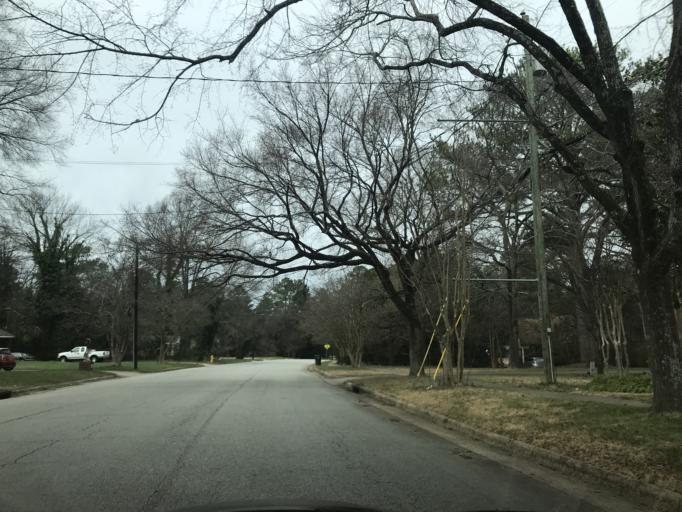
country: US
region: North Carolina
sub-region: Wake County
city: Raleigh
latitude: 35.7813
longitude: -78.6098
